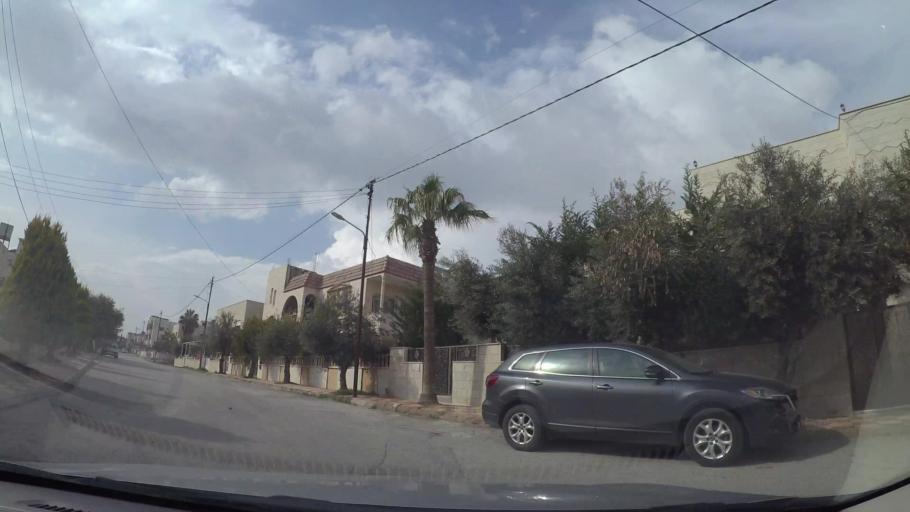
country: JO
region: Amman
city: Umm as Summaq
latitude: 31.8867
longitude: 35.8698
